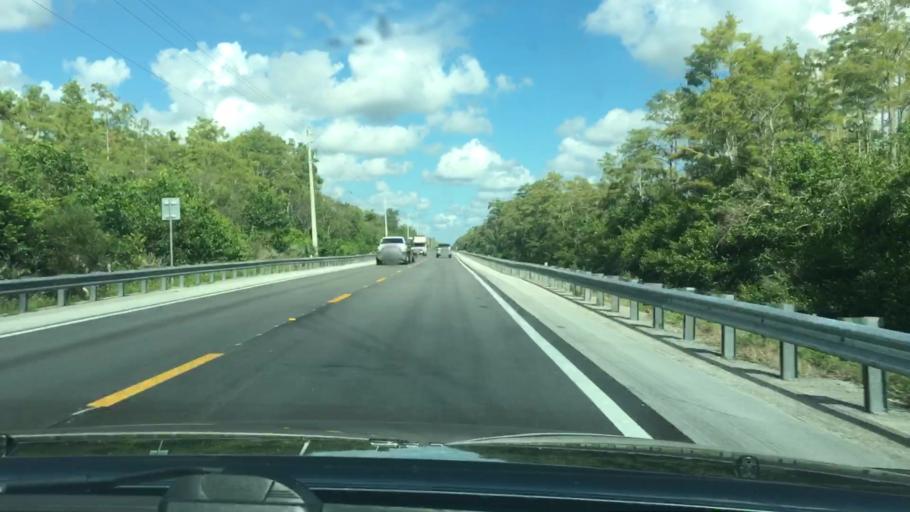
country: US
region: Florida
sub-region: Miami-Dade County
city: Kendall West
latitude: 25.7676
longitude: -80.8342
